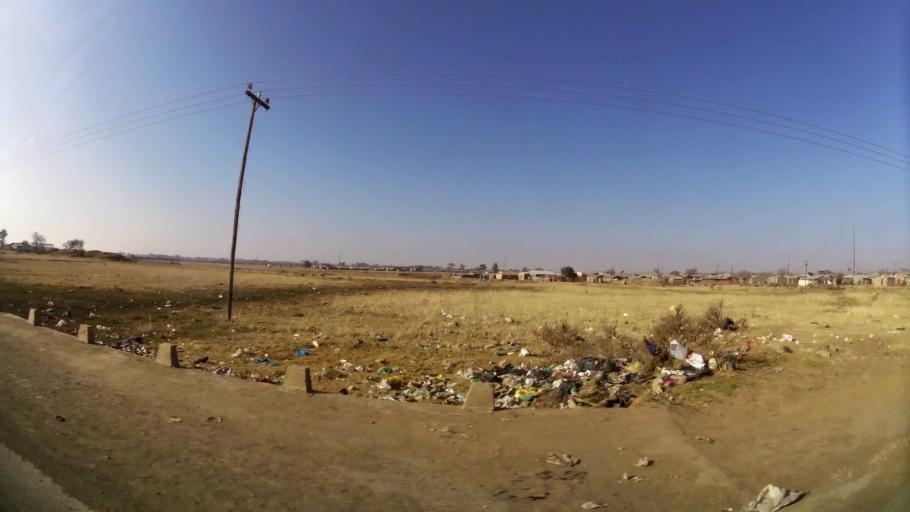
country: ZA
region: Orange Free State
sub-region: Mangaung Metropolitan Municipality
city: Bloemfontein
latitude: -29.1969
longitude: 26.2636
